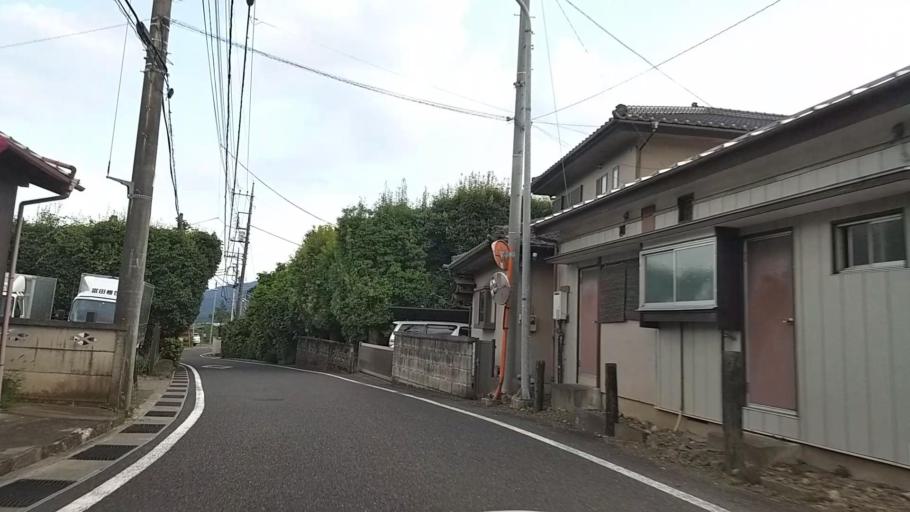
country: JP
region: Yamanashi
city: Uenohara
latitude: 35.6228
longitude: 139.1219
